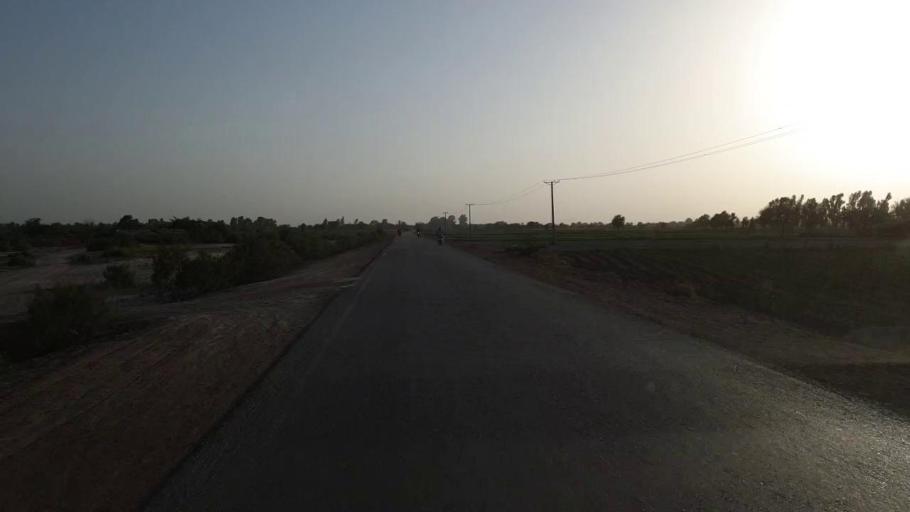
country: PK
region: Sindh
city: Jam Sahib
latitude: 26.2780
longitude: 68.5676
